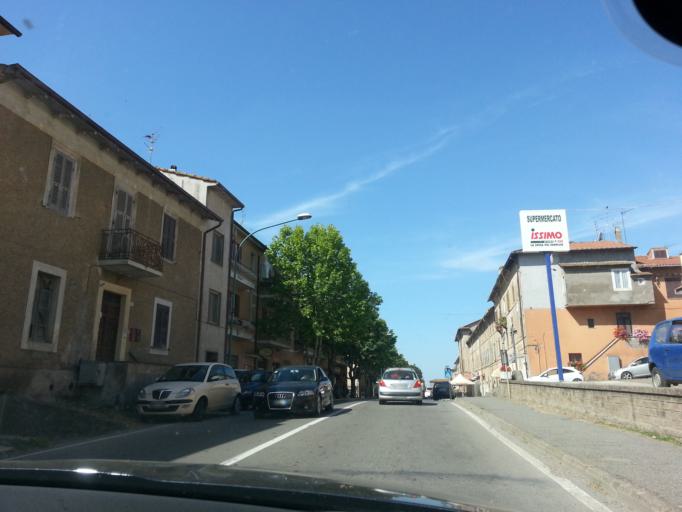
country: IT
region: Latium
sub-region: Provincia di Viterbo
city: Monte Romano
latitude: 42.2694
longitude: 11.9012
